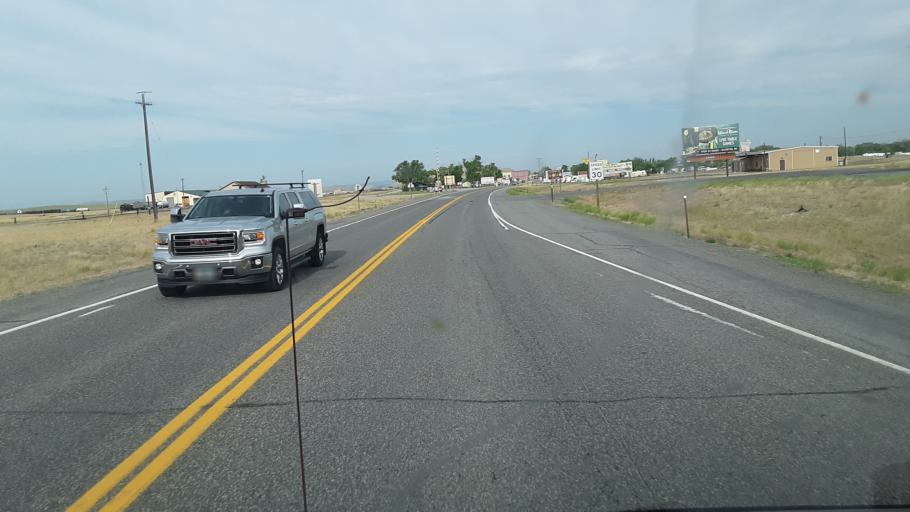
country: US
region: Wyoming
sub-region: Fremont County
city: Riverton
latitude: 43.2357
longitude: -108.0996
